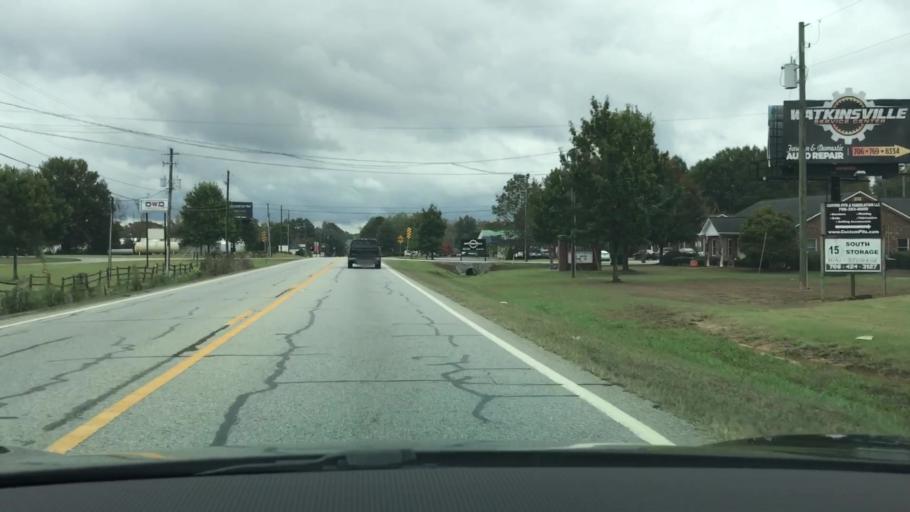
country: US
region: Georgia
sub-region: Oconee County
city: Watkinsville
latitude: 33.8544
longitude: -83.4004
